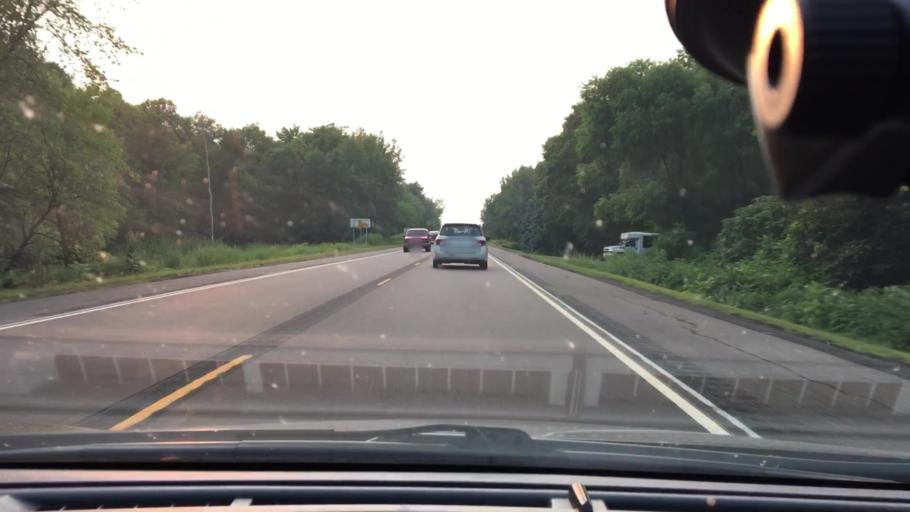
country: US
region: Minnesota
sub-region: Mille Lacs County
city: Vineland
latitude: 46.1460
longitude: -93.7260
